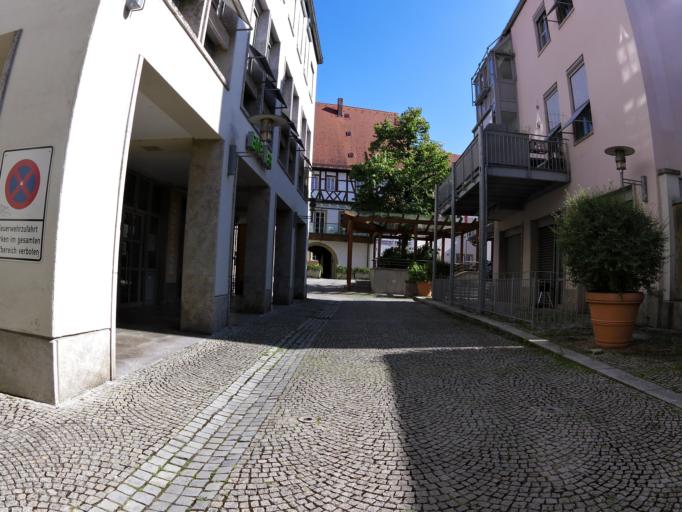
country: DE
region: Bavaria
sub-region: Regierungsbezirk Unterfranken
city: Kitzingen
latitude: 49.7376
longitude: 10.1610
